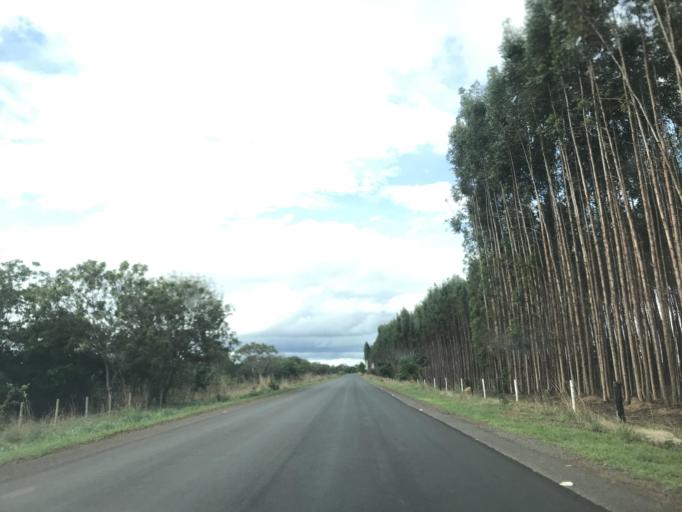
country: BR
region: Goias
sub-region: Bela Vista De Goias
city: Bela Vista de Goias
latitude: -16.9876
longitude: -48.6688
